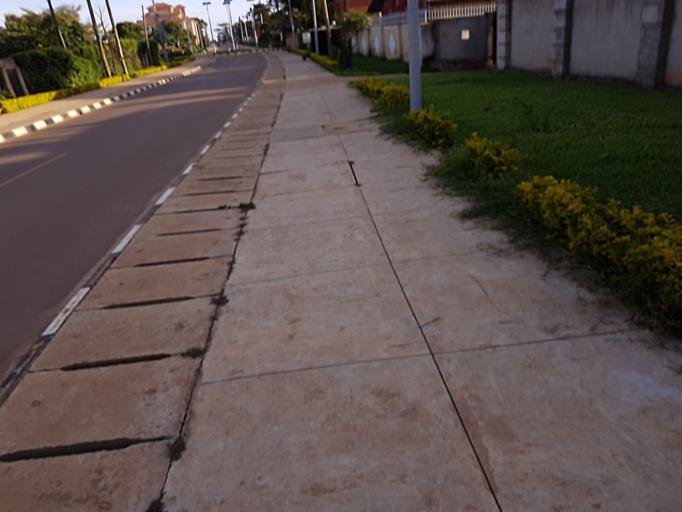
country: UG
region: Central Region
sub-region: Wakiso District
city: Entebbe
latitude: 0.0501
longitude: 32.4649
